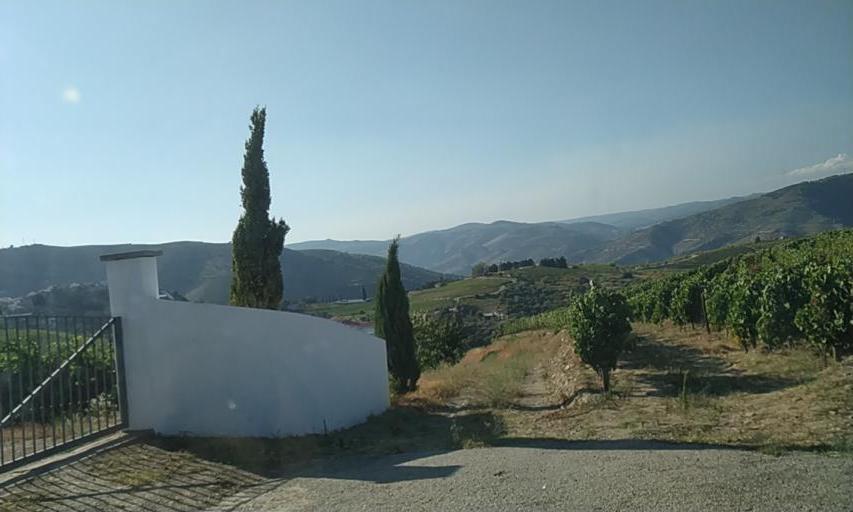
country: PT
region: Viseu
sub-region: Sao Joao da Pesqueira
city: Sao Joao da Pesqueira
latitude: 41.1821
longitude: -7.4026
